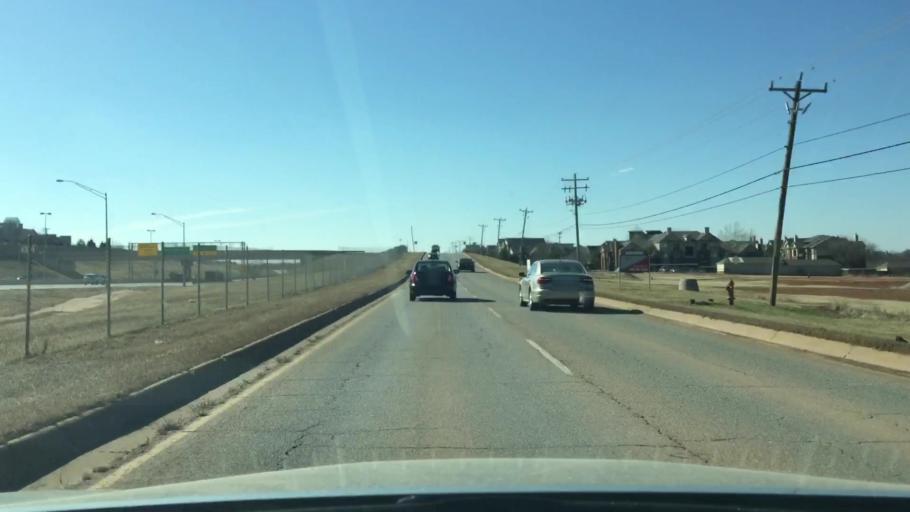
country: US
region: Oklahoma
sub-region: Oklahoma County
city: The Village
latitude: 35.6102
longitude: -97.5912
